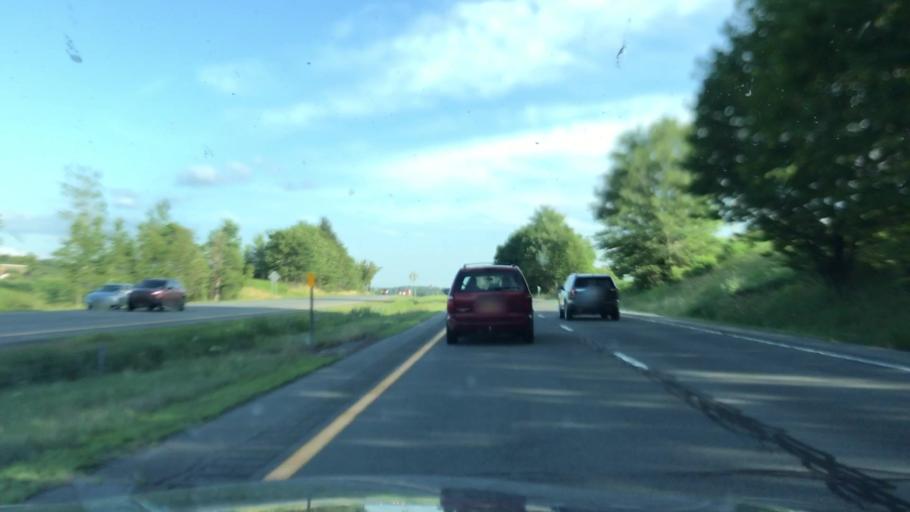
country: US
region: New York
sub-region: Sullivan County
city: Liberty
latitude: 41.7421
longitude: -74.7328
